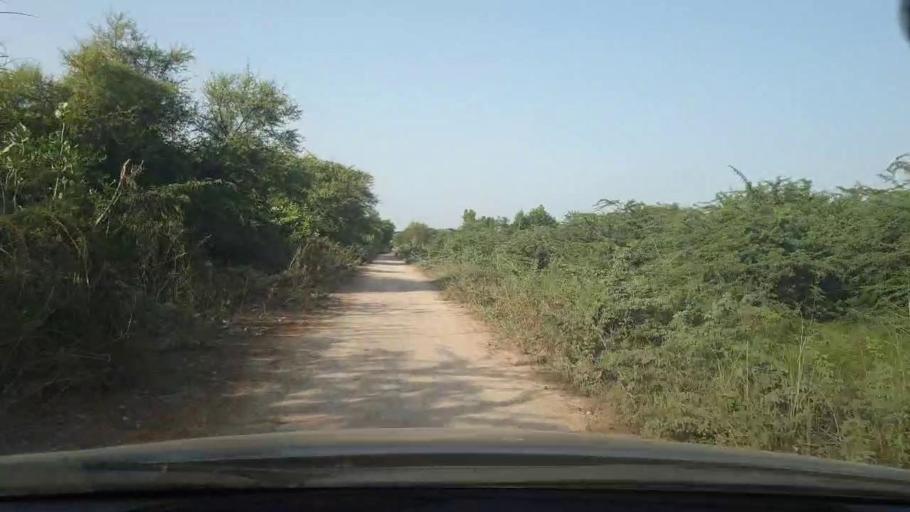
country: PK
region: Sindh
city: Naukot
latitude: 24.7816
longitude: 69.2344
